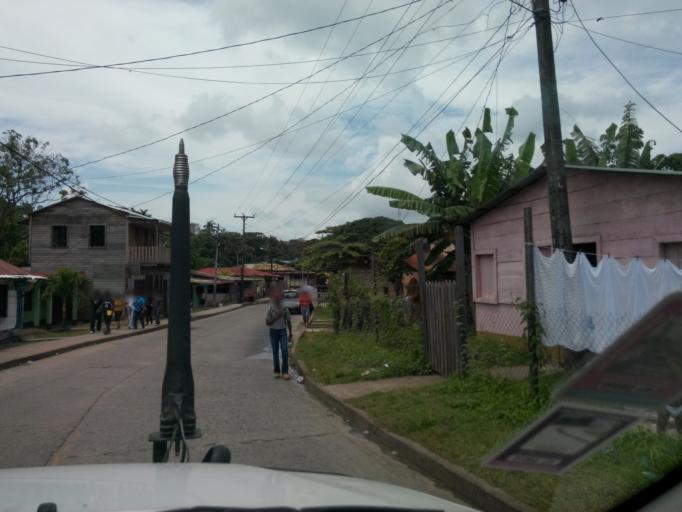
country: NI
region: Atlantico Sur
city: Bluefields
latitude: 12.0083
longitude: -83.7702
